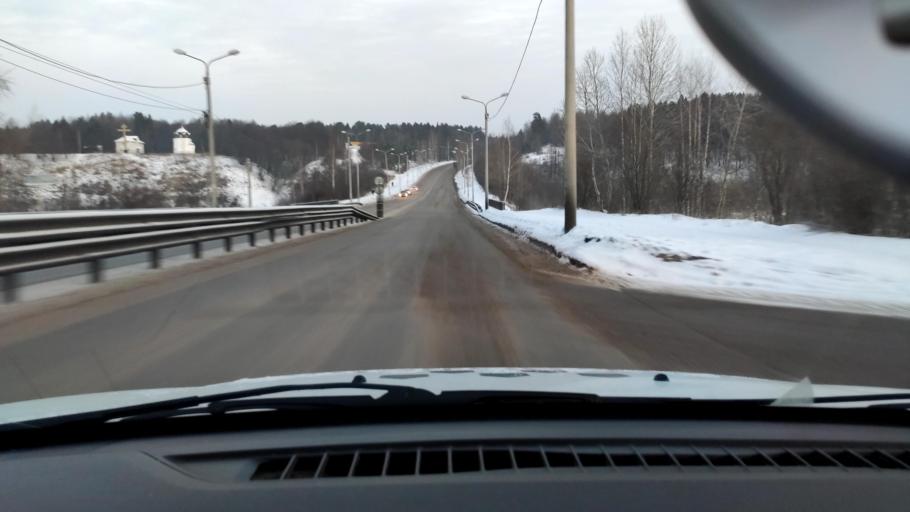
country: RU
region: Perm
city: Perm
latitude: 58.0699
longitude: 56.3670
